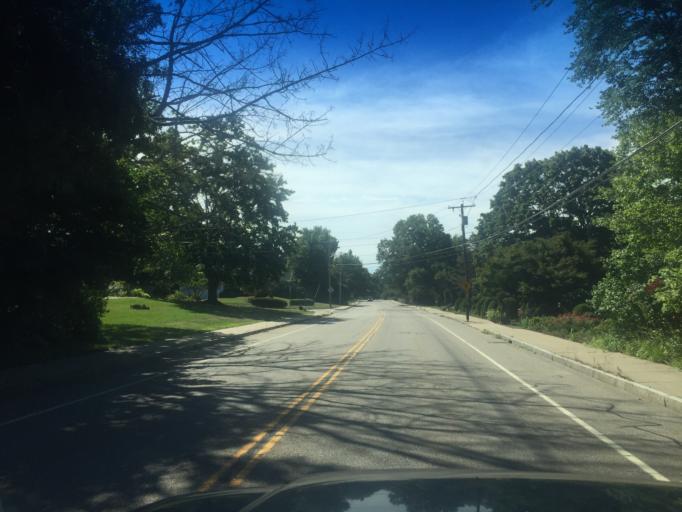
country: US
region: Massachusetts
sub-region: Norfolk County
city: Franklin
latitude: 42.1011
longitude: -71.4281
